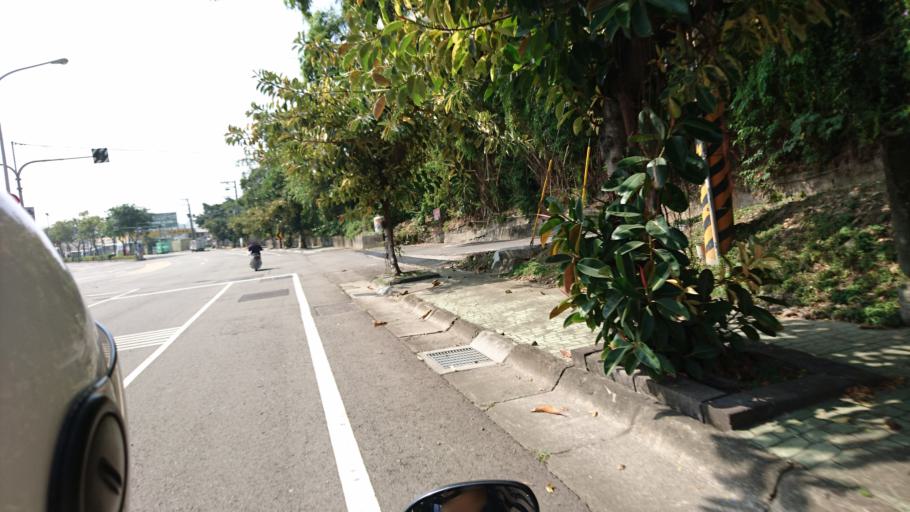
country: TW
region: Taiwan
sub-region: Hsinchu
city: Hsinchu
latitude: 24.7037
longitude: 120.9226
